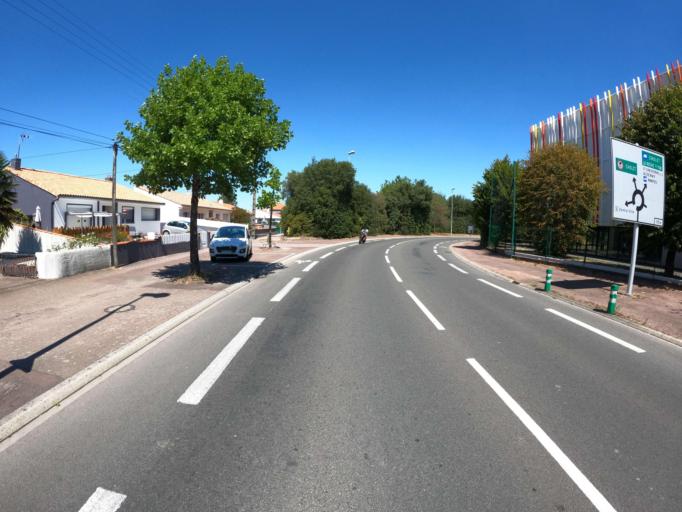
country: FR
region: Pays de la Loire
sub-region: Departement de la Vendee
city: Challans
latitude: 46.8405
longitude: -1.8649
